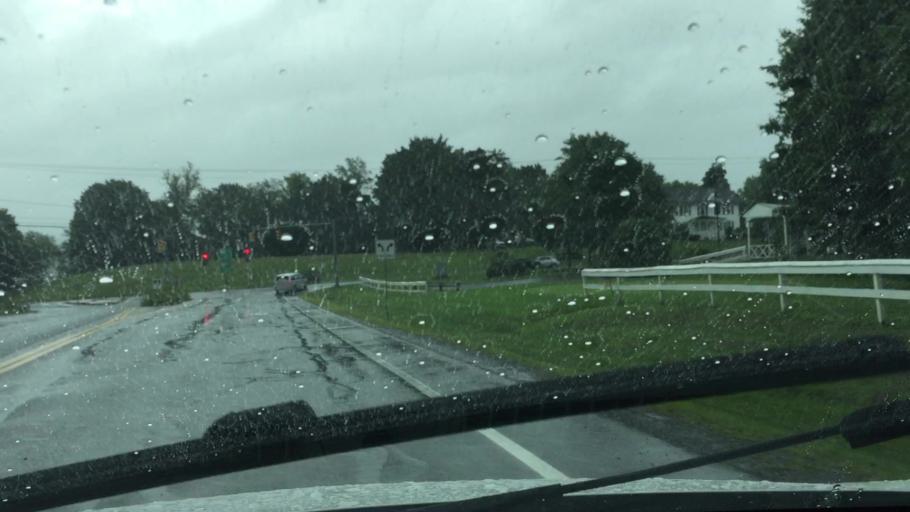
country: US
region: Massachusetts
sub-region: Berkshire County
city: Lanesborough
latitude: 42.4965
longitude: -73.2361
